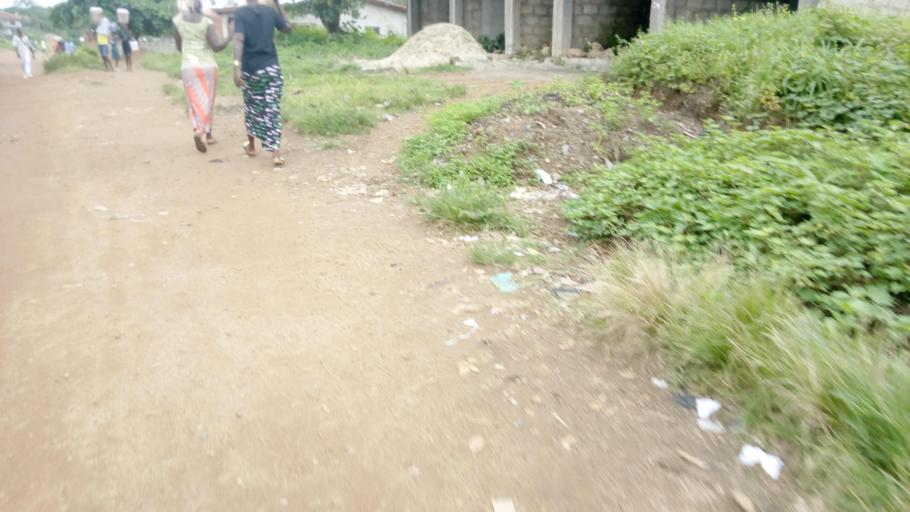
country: SL
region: Northern Province
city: Makeni
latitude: 8.8957
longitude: -12.0316
